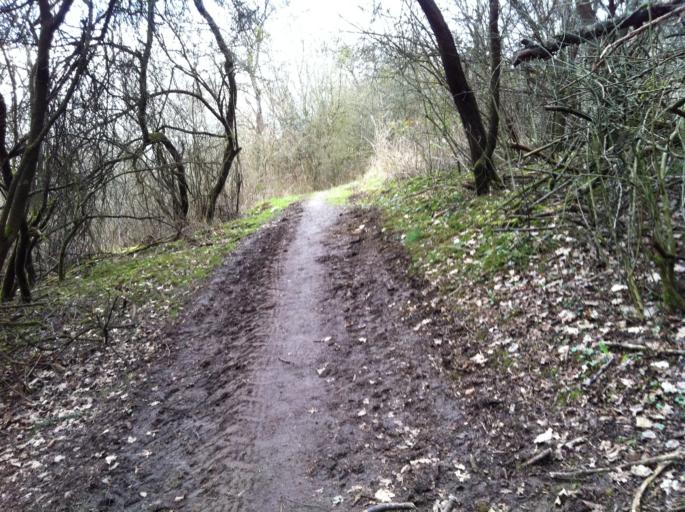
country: DE
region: Hesse
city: Michelstadt
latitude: 49.6751
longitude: 9.0210
